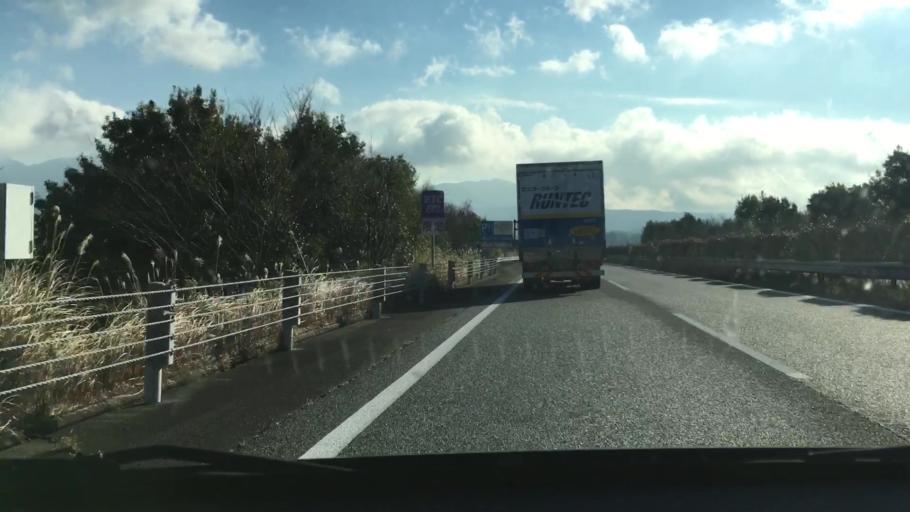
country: JP
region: Kumamoto
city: Hitoyoshi
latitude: 32.0571
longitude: 130.8027
